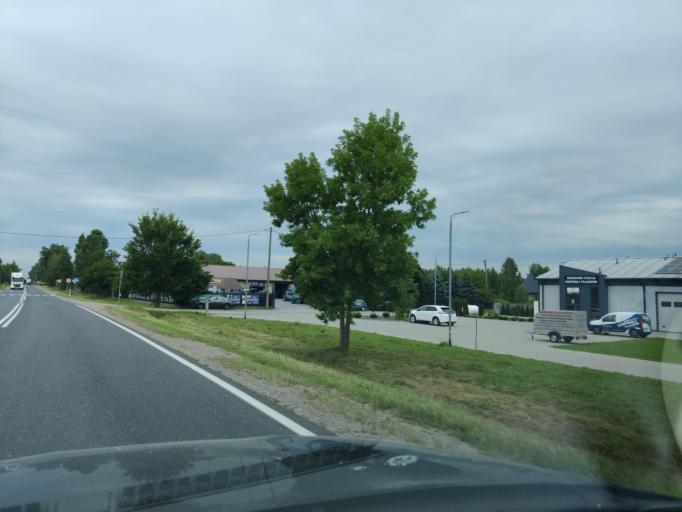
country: PL
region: Masovian Voivodeship
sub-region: Powiat minski
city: Stanislawow
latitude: 52.2917
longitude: 21.5548
